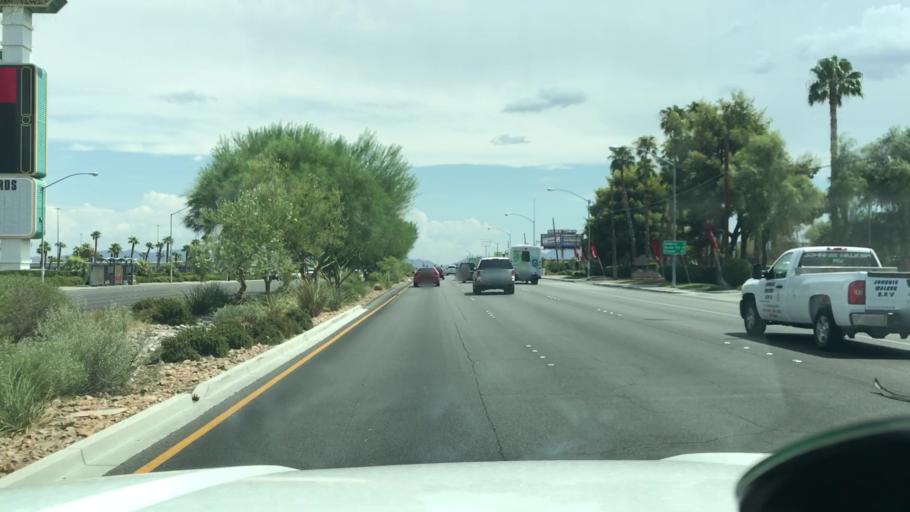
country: US
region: Nevada
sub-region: Clark County
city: Winchester
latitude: 36.1330
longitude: -115.0873
